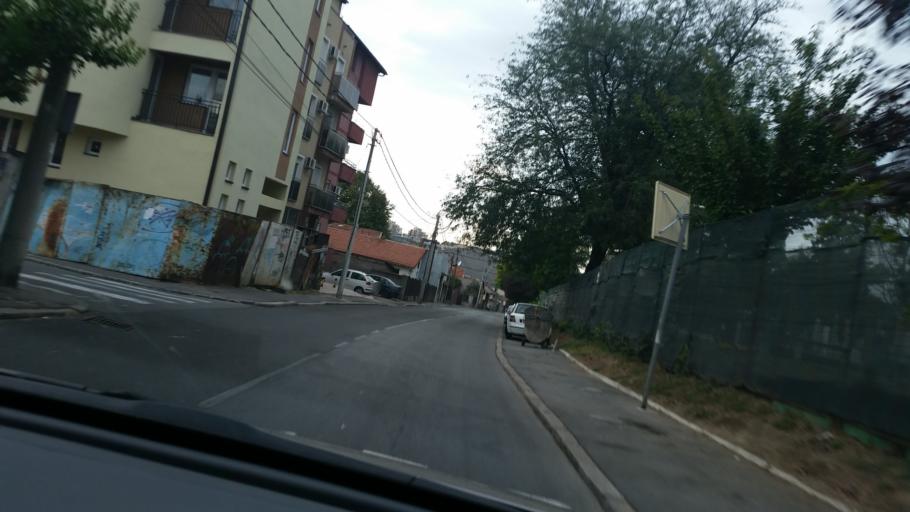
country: RS
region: Central Serbia
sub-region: Belgrade
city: Vracar
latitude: 44.8067
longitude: 20.4876
